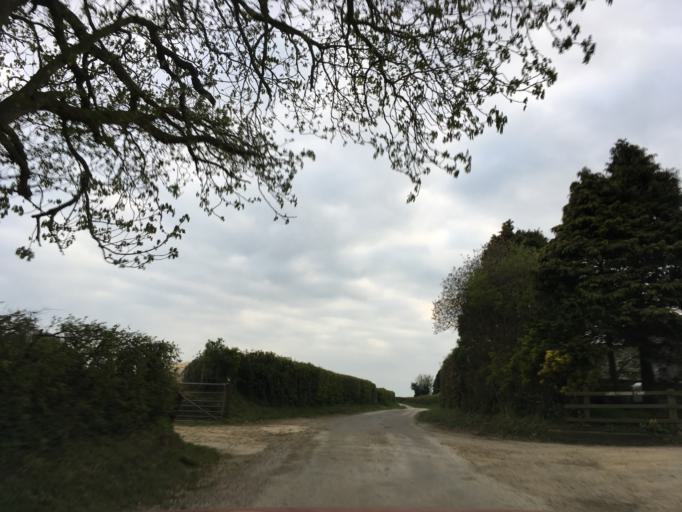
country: GB
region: England
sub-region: Gloucestershire
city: Wotton-under-Edge
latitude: 51.5954
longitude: -2.3383
